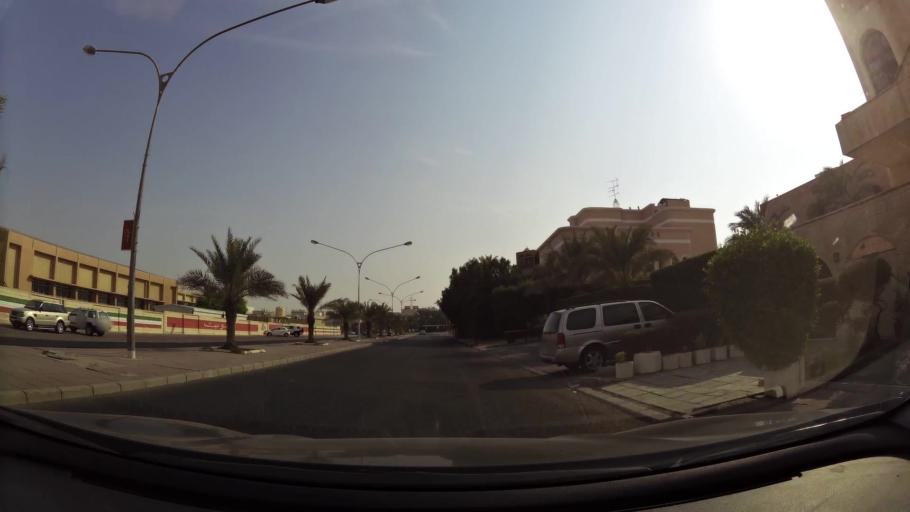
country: KW
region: Al Asimah
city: Ash Shamiyah
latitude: 29.3117
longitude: 47.9842
